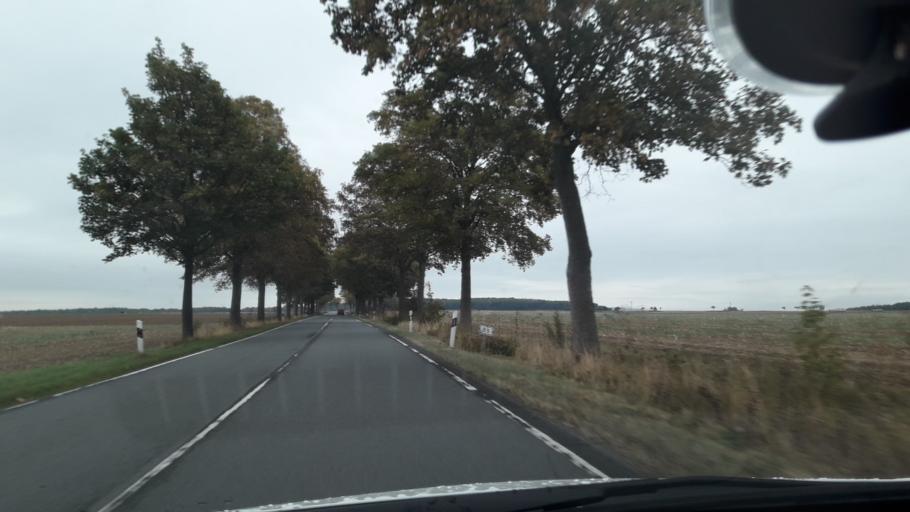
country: DE
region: Lower Saxony
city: Gielde
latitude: 52.0201
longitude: 10.4875
